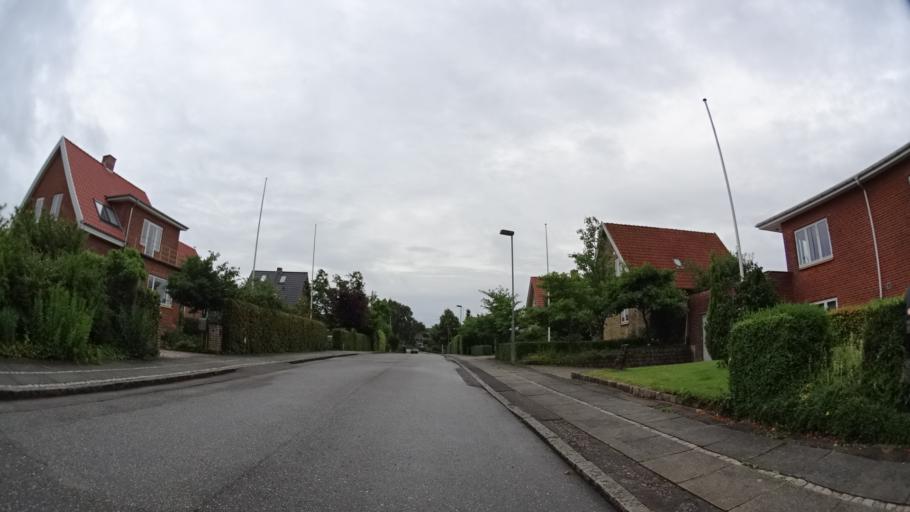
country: DK
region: Central Jutland
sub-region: Arhus Kommune
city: Arhus
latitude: 56.1257
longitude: 10.1801
